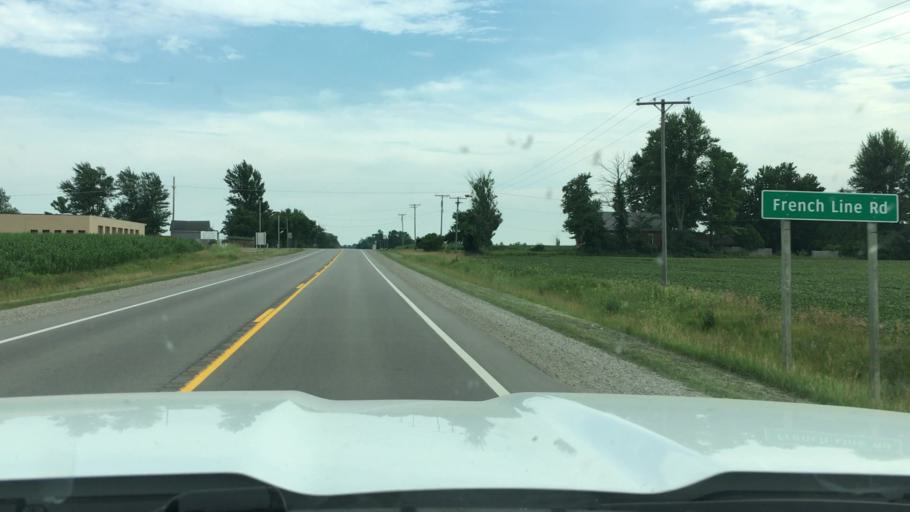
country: US
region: Michigan
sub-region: Sanilac County
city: Marlette
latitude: 43.3586
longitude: -83.0851
